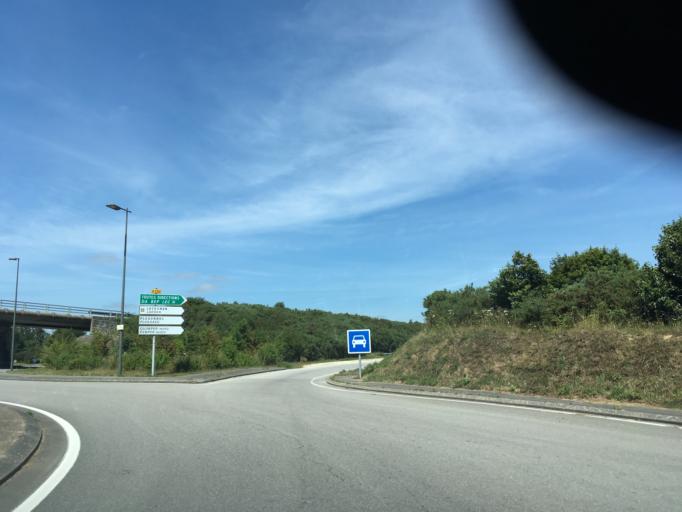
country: FR
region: Brittany
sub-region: Departement du Finistere
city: Quimper
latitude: 48.0124
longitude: -4.1204
